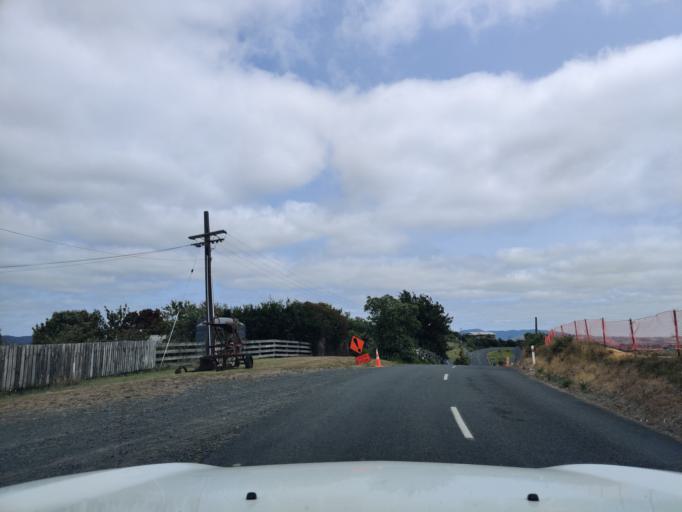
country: NZ
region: Waikato
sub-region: Waikato District
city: Te Kauwhata
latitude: -37.5196
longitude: 175.1773
